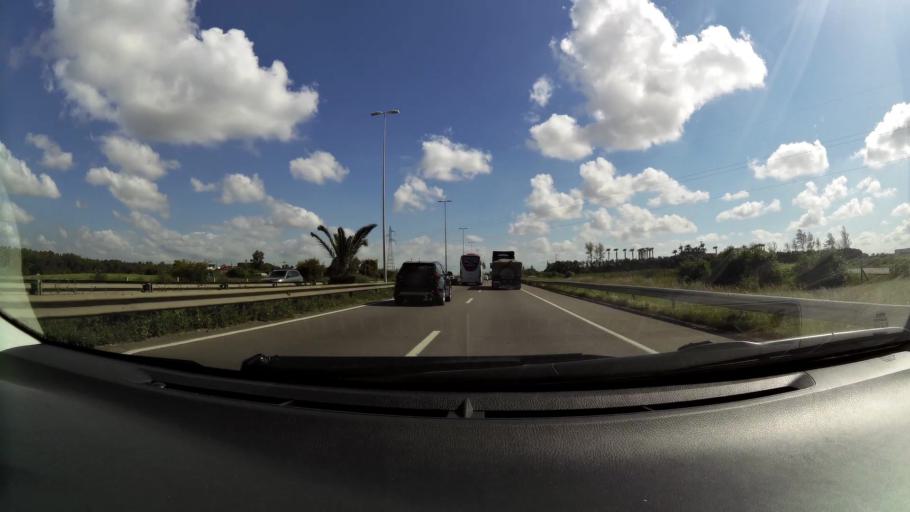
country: MA
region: Grand Casablanca
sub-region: Nouaceur
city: Bouskoura
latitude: 33.4591
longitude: -7.6335
